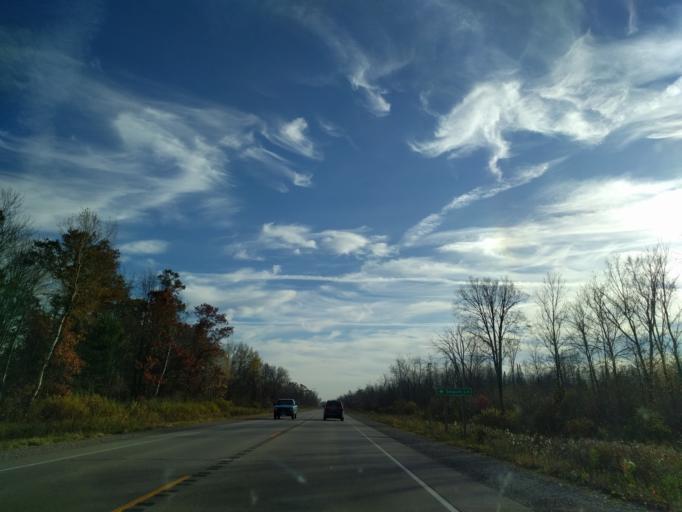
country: US
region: Wisconsin
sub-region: Marinette County
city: Peshtigo
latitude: 45.2433
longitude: -87.9944
